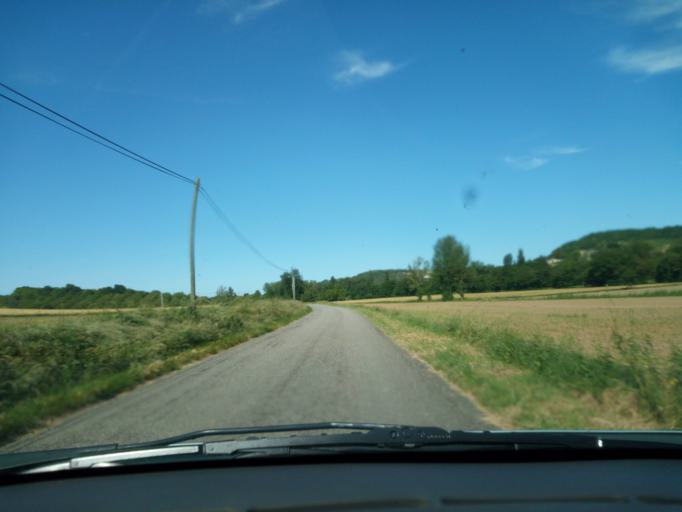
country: FR
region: Midi-Pyrenees
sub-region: Departement du Lot
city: Castelnau-Montratier
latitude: 44.2358
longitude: 1.3345
